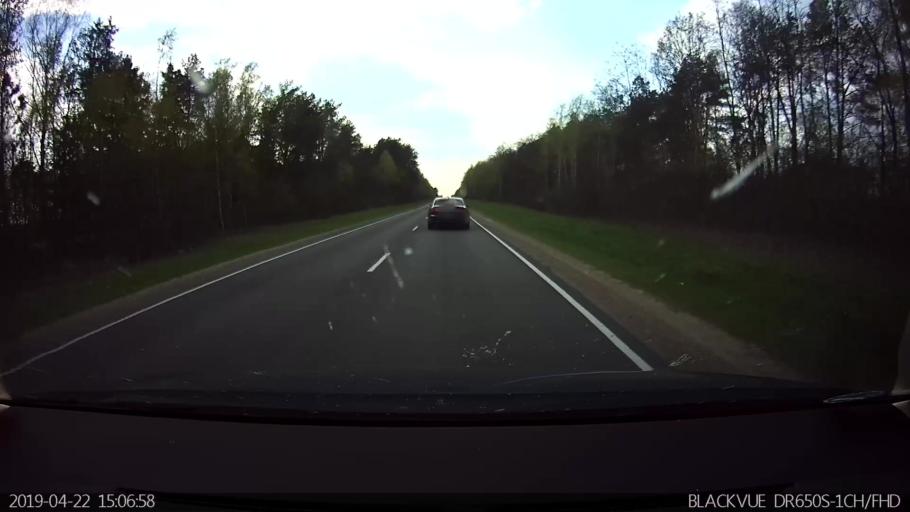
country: BY
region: Brest
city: Kamyanyets
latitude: 52.3301
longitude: 23.8219
